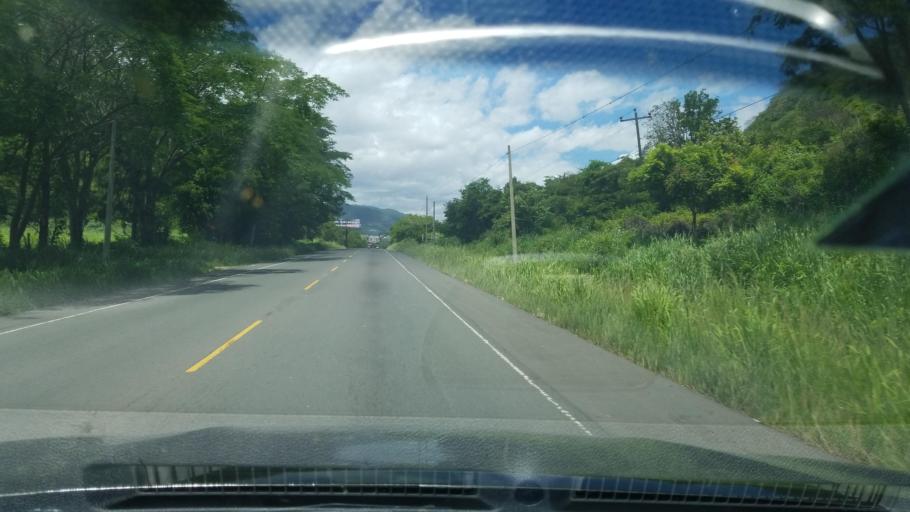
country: HN
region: Francisco Morazan
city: Rio Abajo
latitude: 14.1905
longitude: -87.2041
